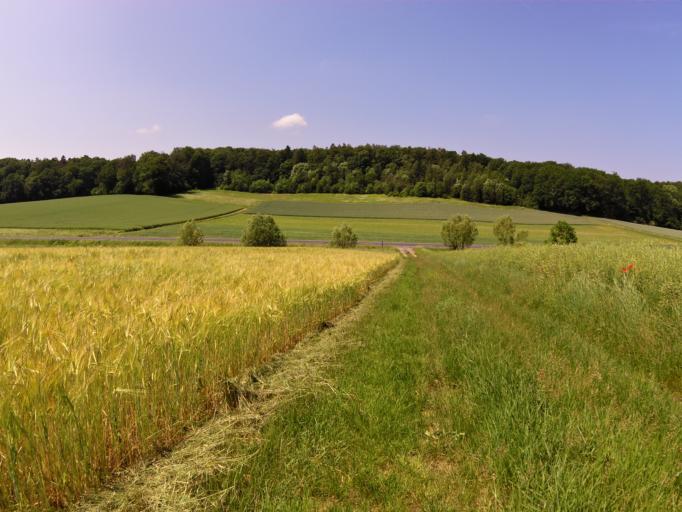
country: DE
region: Bavaria
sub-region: Regierungsbezirk Unterfranken
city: Kleinrinderfeld
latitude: 49.7169
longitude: 9.8437
